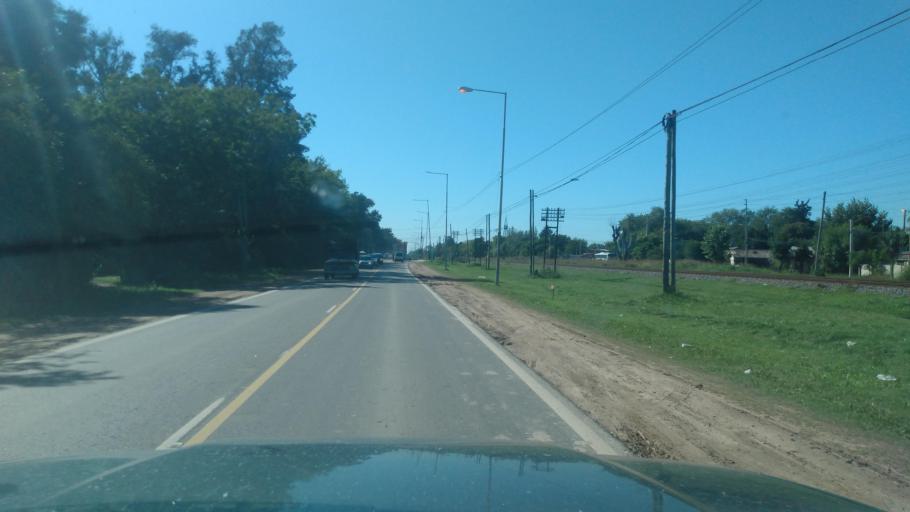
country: AR
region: Buenos Aires
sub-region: Partido de General Rodriguez
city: General Rodriguez
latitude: -34.6002
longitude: -58.9891
